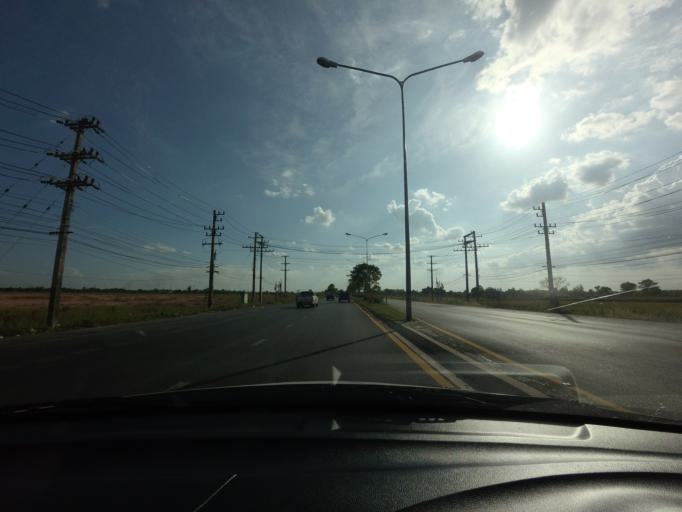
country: TH
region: Nakhon Nayok
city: Nakhon Nayok
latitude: 14.2249
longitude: 101.1774
